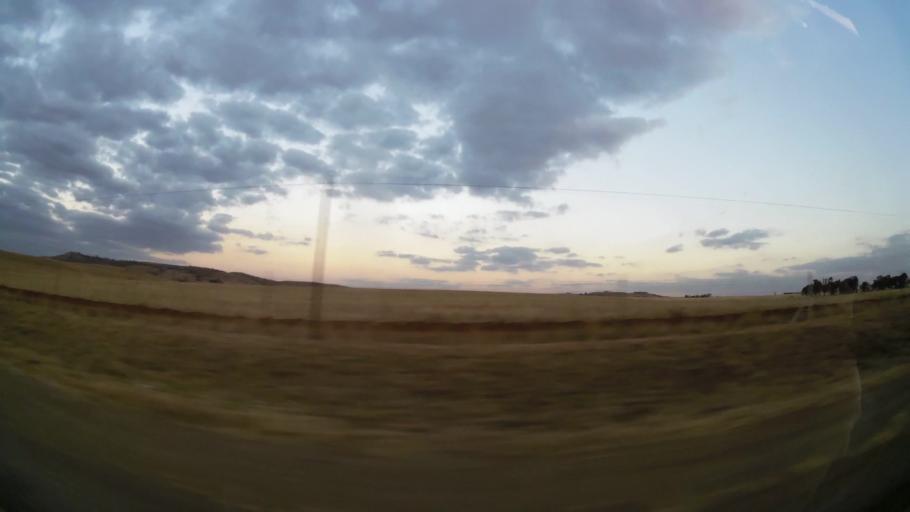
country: ZA
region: Gauteng
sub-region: West Rand District Municipality
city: Krugersdorp
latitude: -26.0556
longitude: 27.7066
